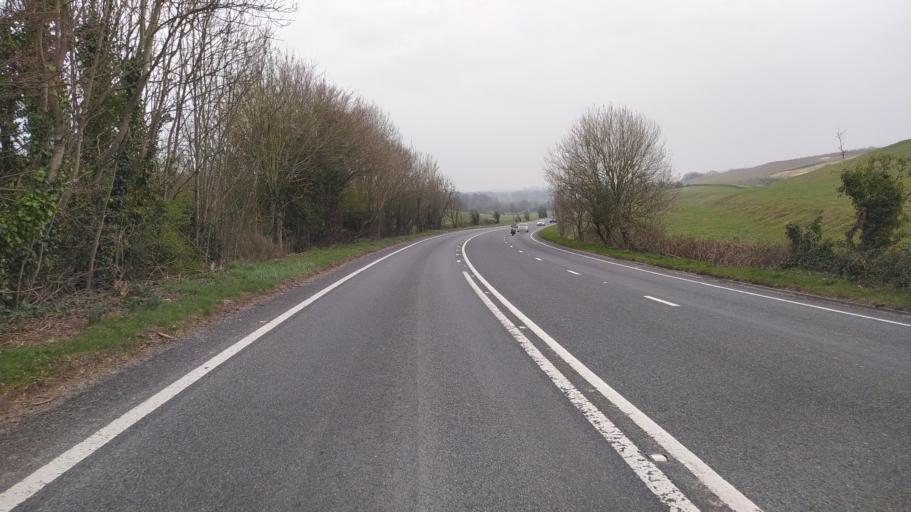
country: GB
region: England
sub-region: Dorset
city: Dorchester
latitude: 50.7178
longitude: -2.4721
